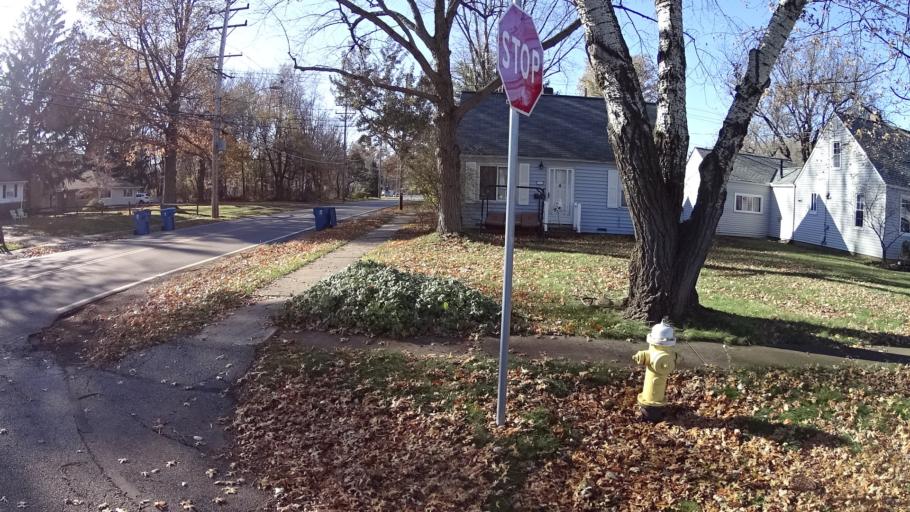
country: US
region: Ohio
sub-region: Lorain County
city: Avon Lake
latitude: 41.5103
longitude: -82.0157
